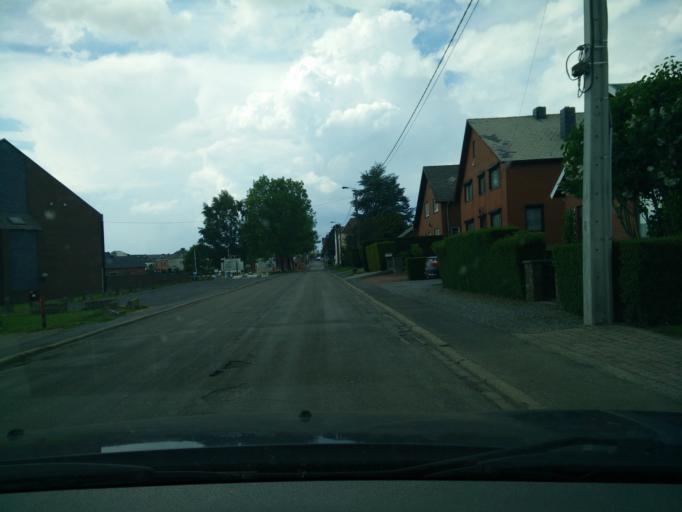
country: BE
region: Wallonia
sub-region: Province de Namur
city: Philippeville
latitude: 50.1928
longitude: 4.5463
